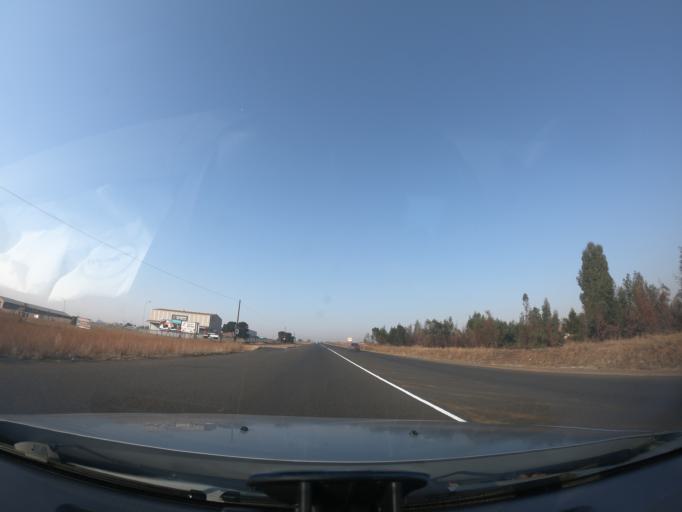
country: ZA
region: Mpumalanga
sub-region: Nkangala District Municipality
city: Middelburg
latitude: -25.8172
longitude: 29.4614
